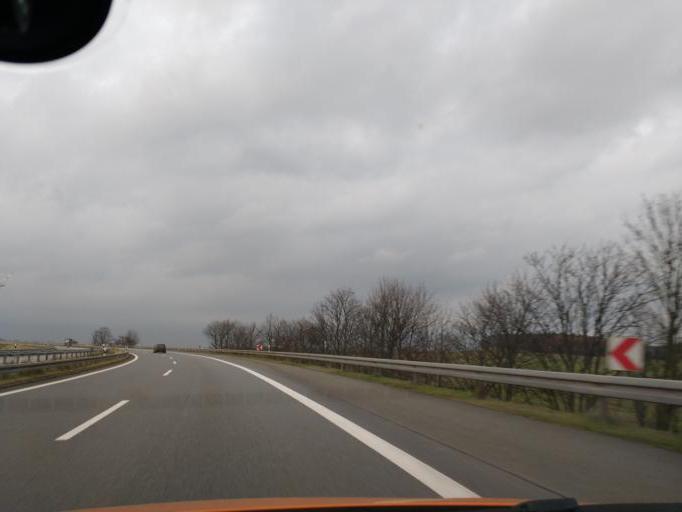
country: DE
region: Brandenburg
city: Wittstock
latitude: 53.1301
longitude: 12.4661
